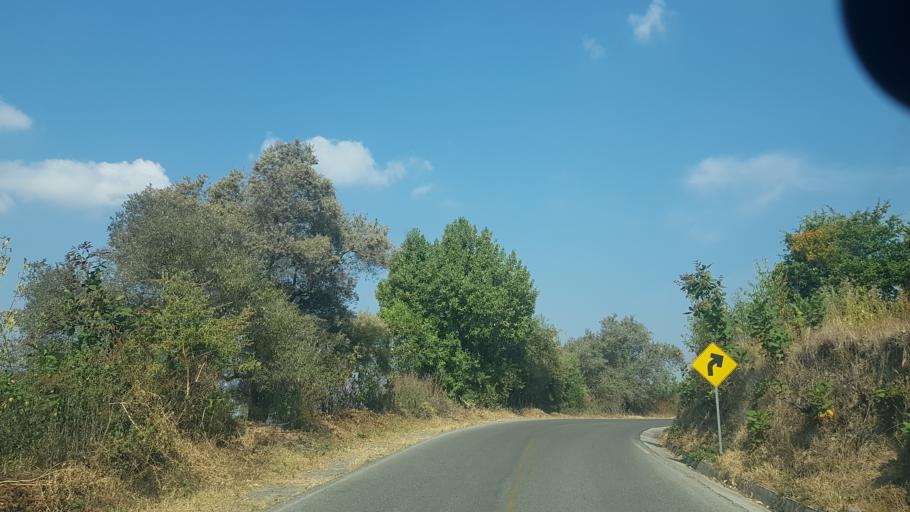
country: MX
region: Puebla
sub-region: Tochimilco
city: Santa Cruz Cuautomatitla
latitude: 18.8901
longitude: -98.6698
